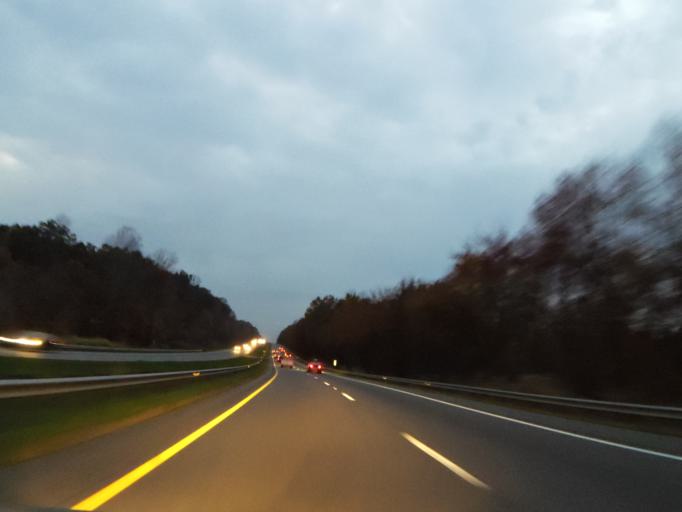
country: US
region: North Carolina
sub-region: McDowell County
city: West Marion
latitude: 35.6357
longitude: -82.0905
